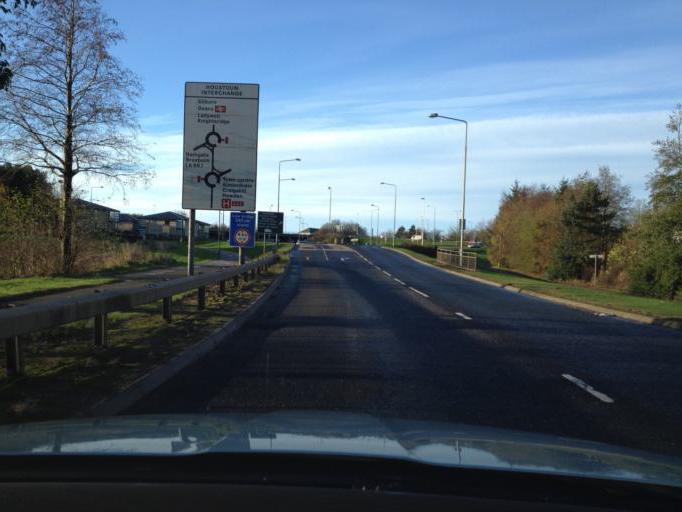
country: GB
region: Scotland
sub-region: West Lothian
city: Livingston
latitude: 55.9072
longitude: -3.5116
